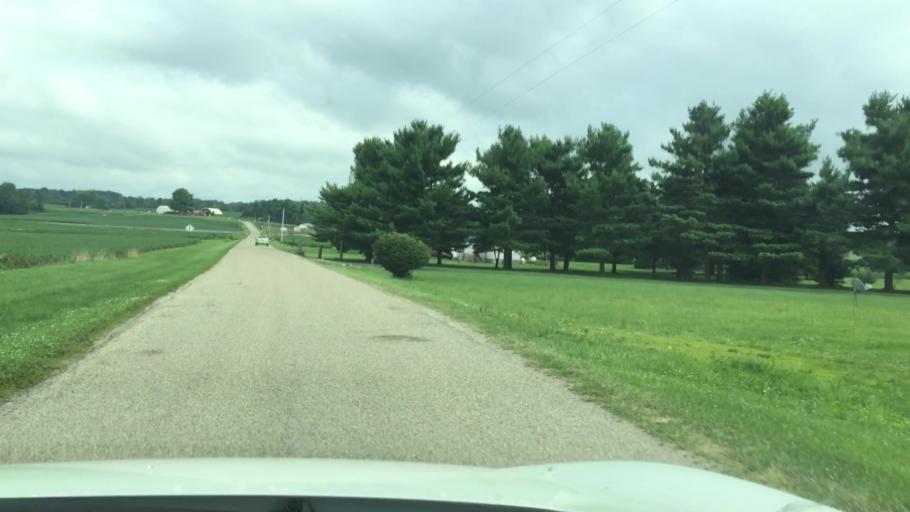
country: US
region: Ohio
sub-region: Champaign County
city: Mechanicsburg
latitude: 40.0508
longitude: -83.6368
